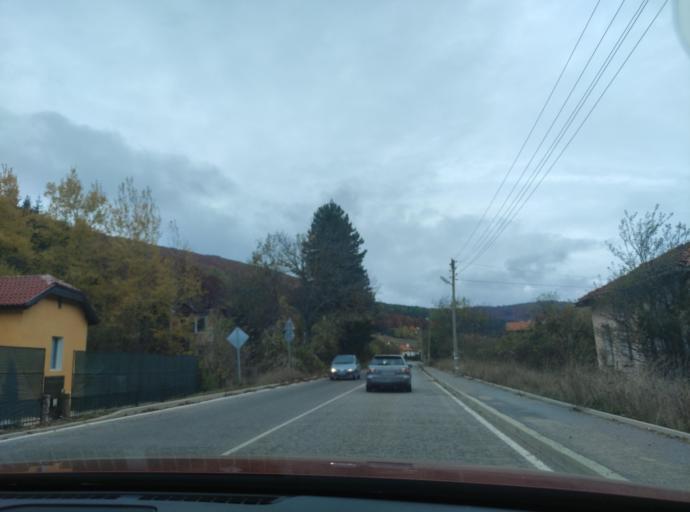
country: BG
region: Sofiya
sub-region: Obshtina Godech
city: Godech
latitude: 43.0881
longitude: 23.0995
